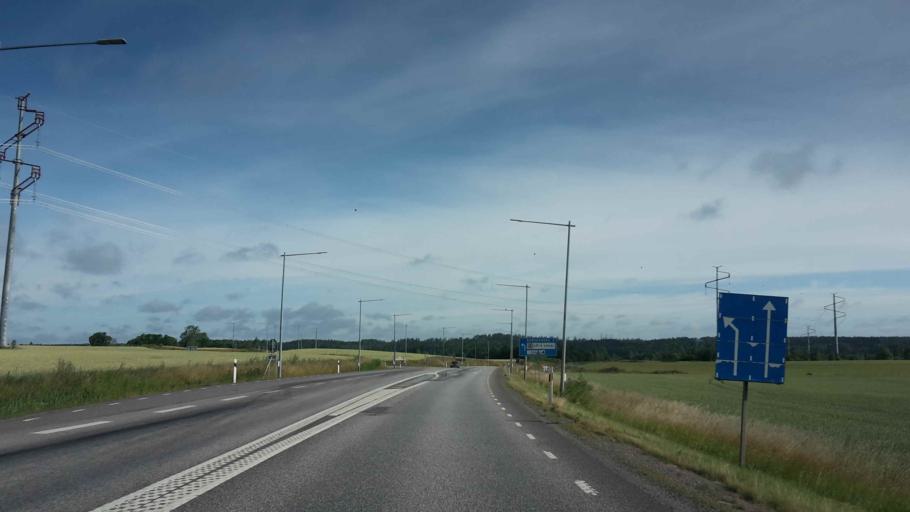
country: SE
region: OEstergoetland
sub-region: Motala Kommun
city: Borensberg
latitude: 58.5439
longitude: 15.3214
